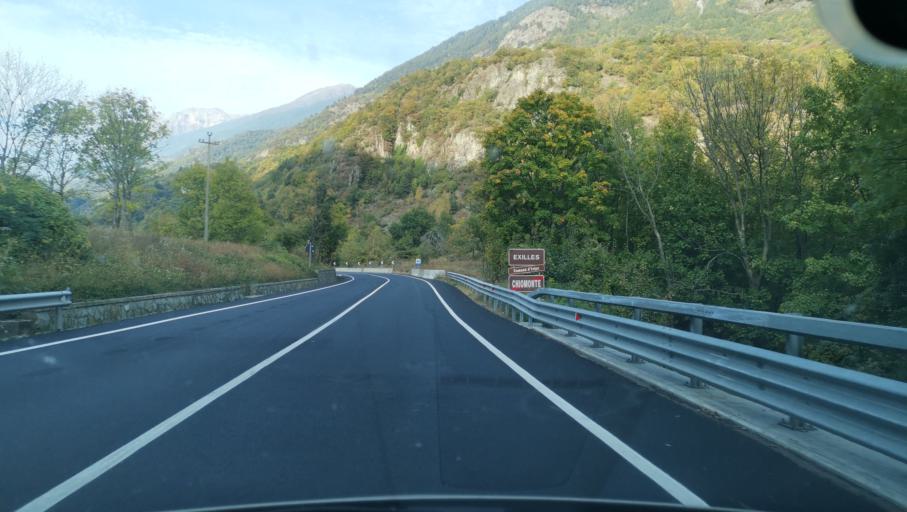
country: IT
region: Piedmont
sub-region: Provincia di Torino
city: Chiomonte
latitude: 45.1090
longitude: 6.9593
